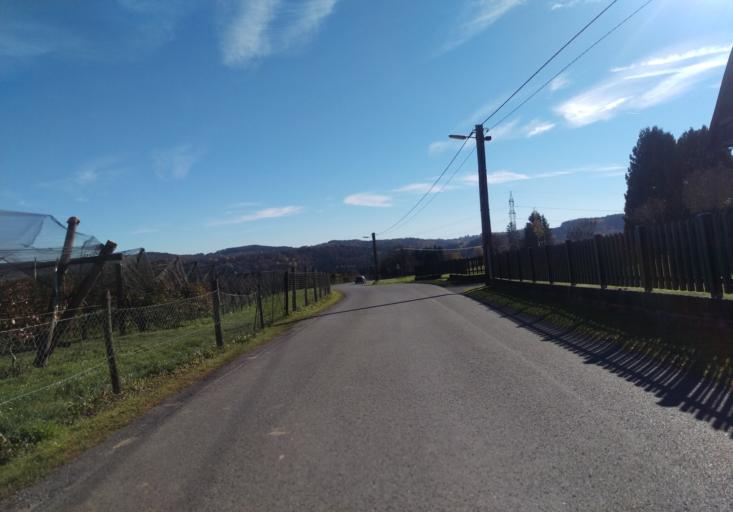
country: AT
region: Styria
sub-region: Graz Stadt
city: Mariatrost
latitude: 47.1192
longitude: 15.4942
